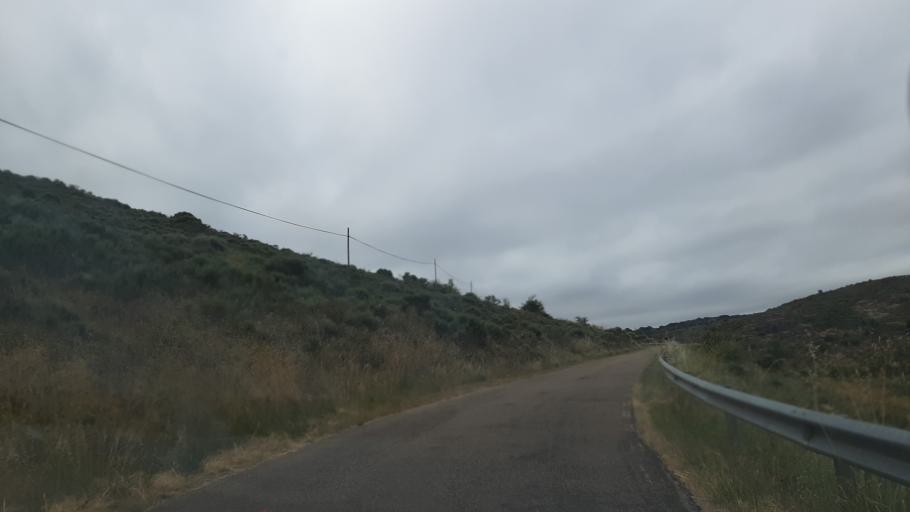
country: ES
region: Castille and Leon
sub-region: Provincia de Salamanca
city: Pastores
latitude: 40.5354
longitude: -6.4842
